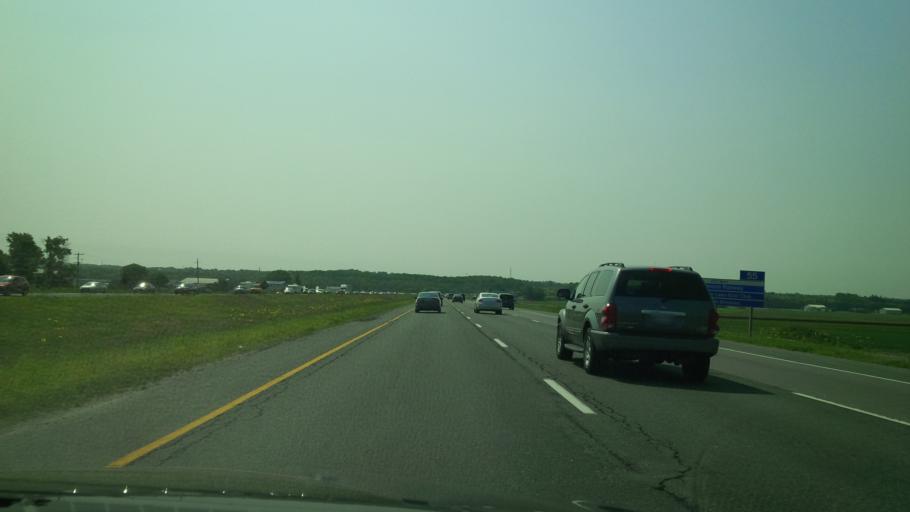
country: CA
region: Ontario
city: Bradford West Gwillimbury
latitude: 44.0452
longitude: -79.6034
